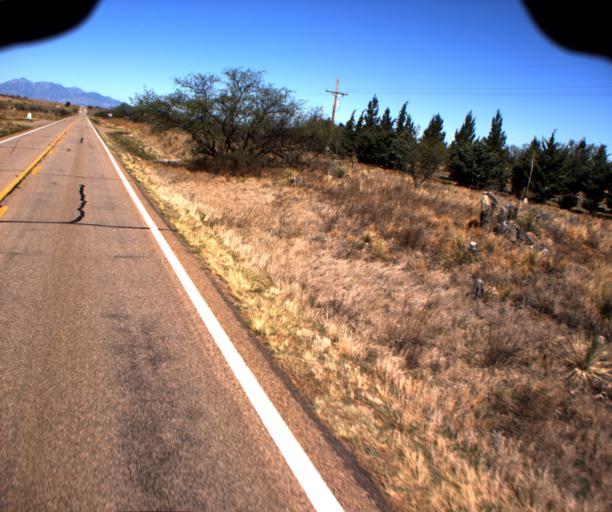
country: US
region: Arizona
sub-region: Cochise County
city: Huachuca City
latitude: 31.7240
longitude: -110.4891
